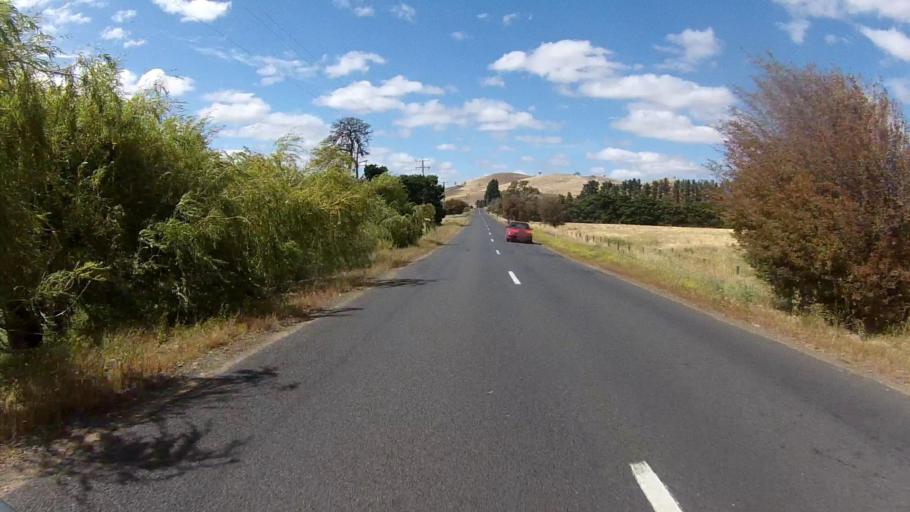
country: AU
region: Tasmania
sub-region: Brighton
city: Bridgewater
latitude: -42.5450
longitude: 147.3737
